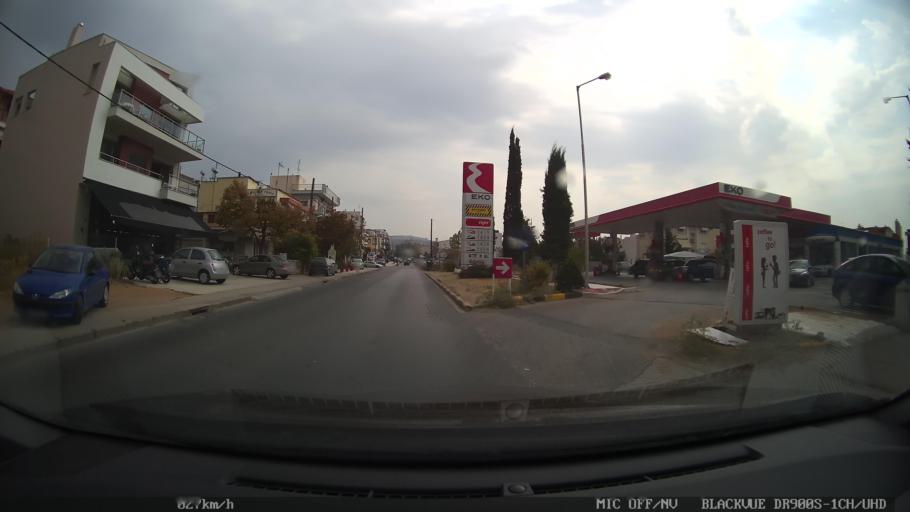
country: GR
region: Central Macedonia
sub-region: Nomos Thessalonikis
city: Pylaia
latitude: 40.6091
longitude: 22.9911
